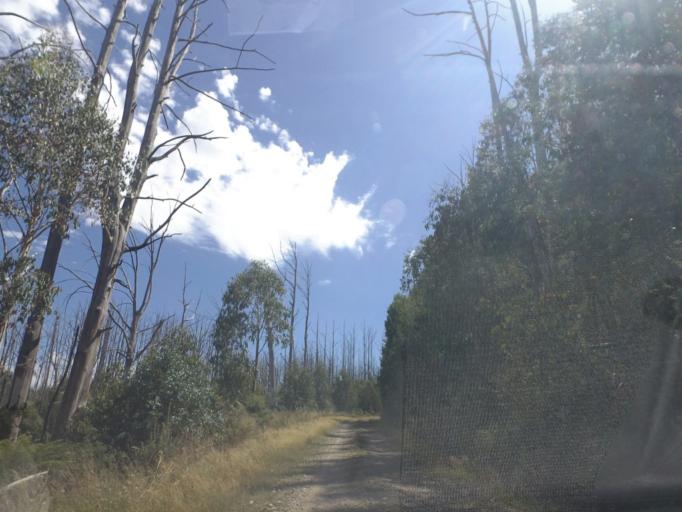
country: AU
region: Victoria
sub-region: Murrindindi
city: Alexandra
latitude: -37.4735
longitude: 145.8367
